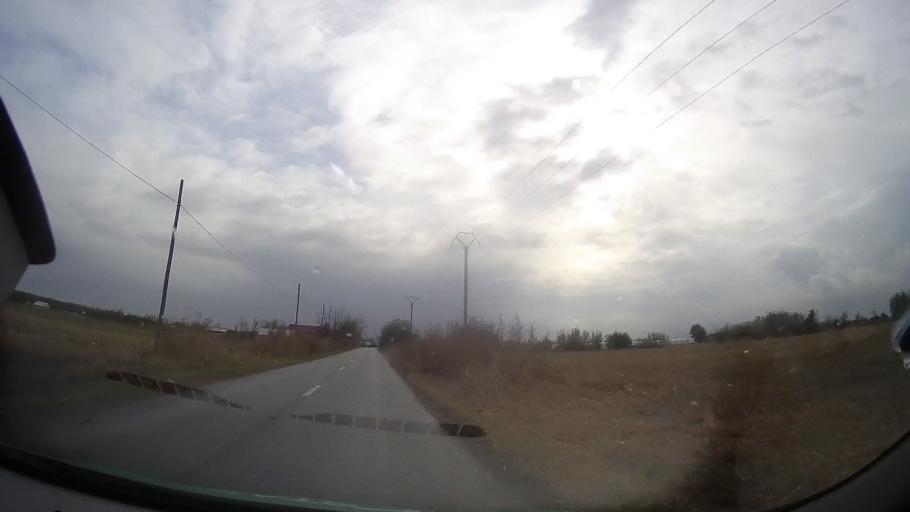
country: RO
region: Ialomita
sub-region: Comuna Fierbinti-Targ
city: Fierbintii de Jos
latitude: 44.7024
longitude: 26.3932
